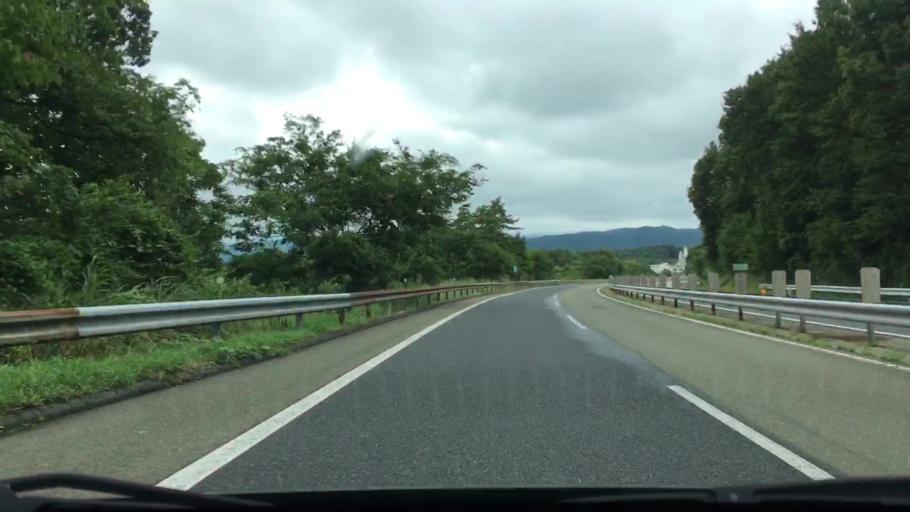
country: JP
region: Hiroshima
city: Shobara
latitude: 34.8314
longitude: 133.0469
